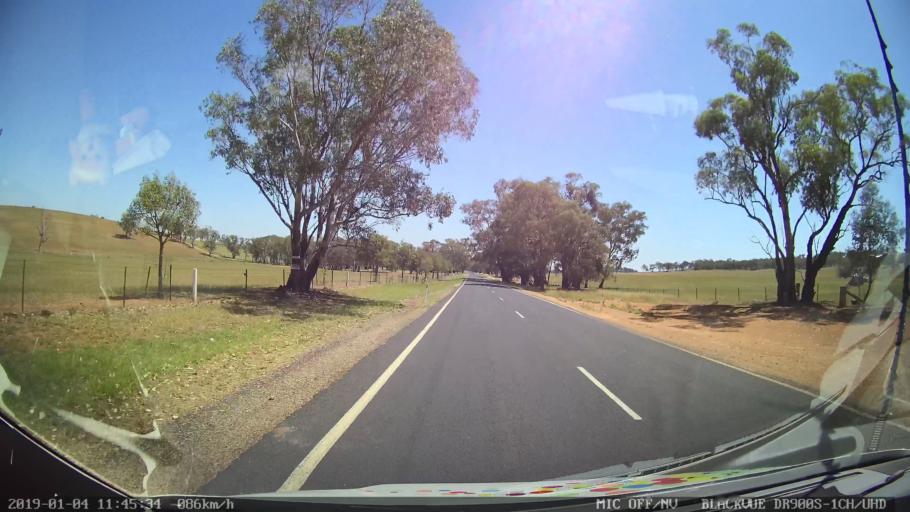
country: AU
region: New South Wales
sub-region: Cabonne
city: Molong
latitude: -32.9521
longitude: 148.7631
